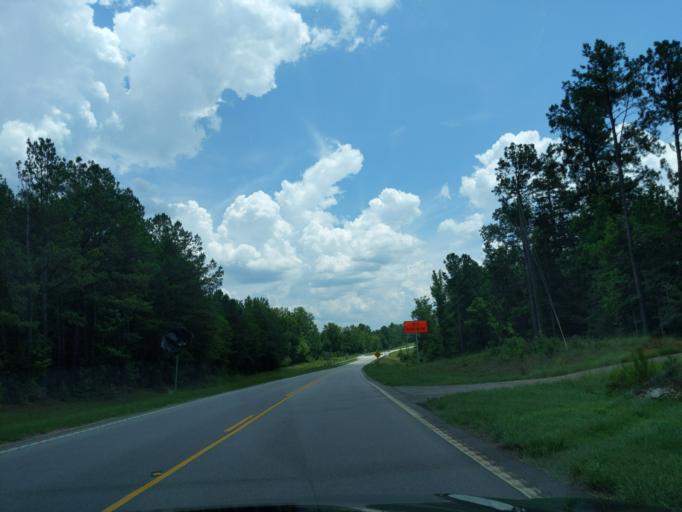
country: US
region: South Carolina
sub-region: Edgefield County
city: Edgefield
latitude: 33.8656
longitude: -81.9889
